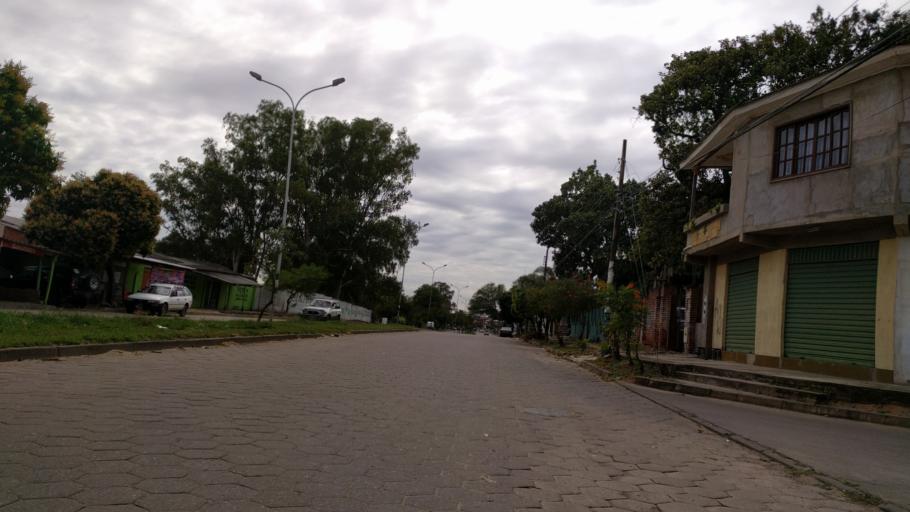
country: BO
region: Santa Cruz
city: Santa Cruz de la Sierra
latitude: -17.8147
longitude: -63.1977
